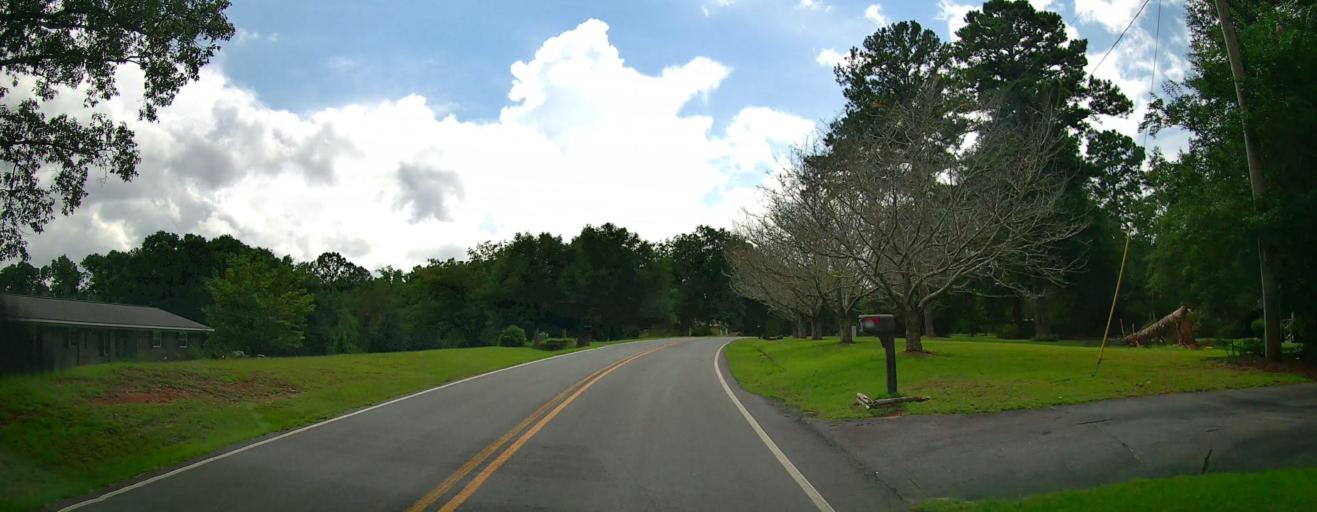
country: US
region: Georgia
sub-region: Houston County
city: Perry
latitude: 32.5181
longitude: -83.7198
